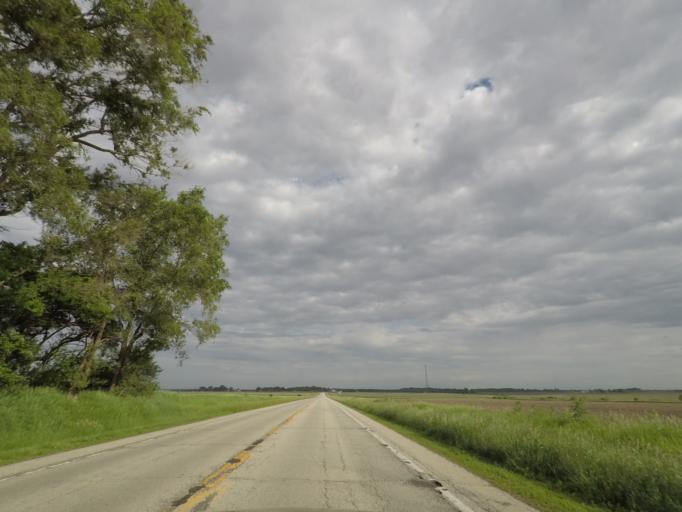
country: US
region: Illinois
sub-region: Logan County
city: Lincoln
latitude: 40.0966
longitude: -89.3152
